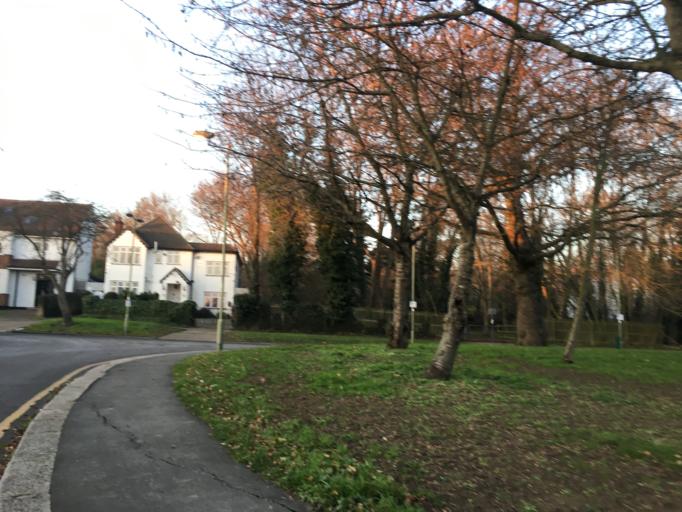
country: GB
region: England
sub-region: Greater London
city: Hendon
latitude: 51.6115
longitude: -0.2257
